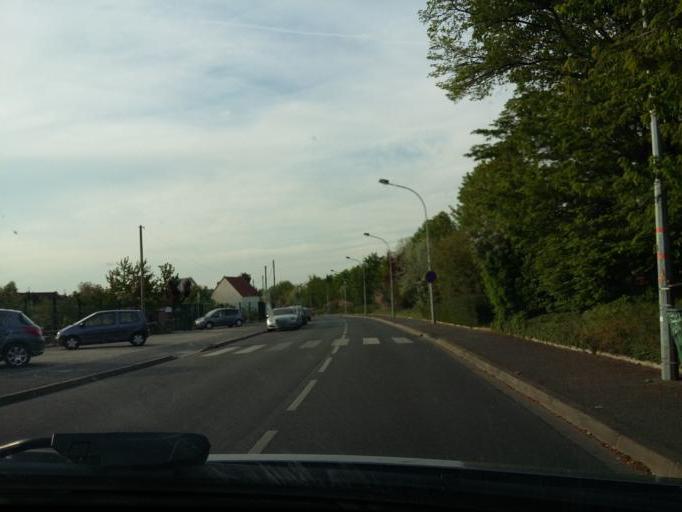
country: FR
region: Ile-de-France
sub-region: Departement du Val-d'Oise
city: Ermont
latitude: 48.9811
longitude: 2.2618
